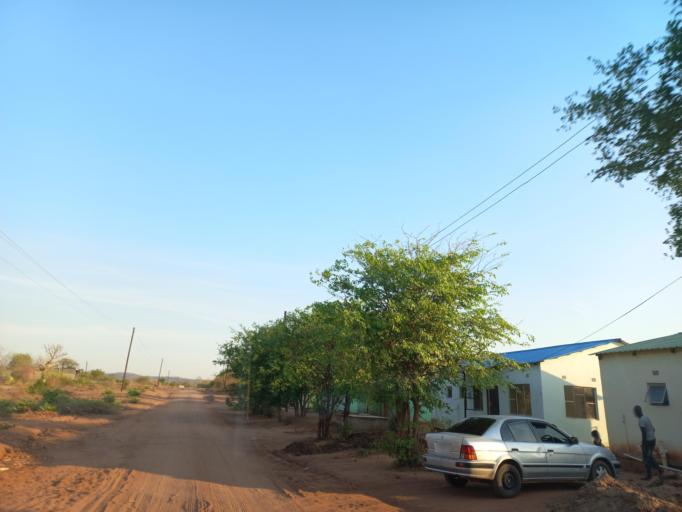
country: ZM
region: Lusaka
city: Luangwa
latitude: -15.6202
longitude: 30.3904
